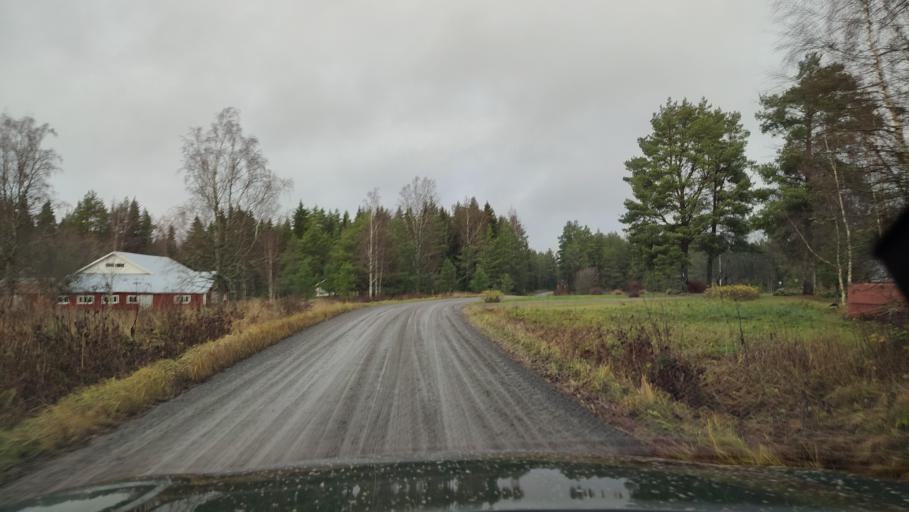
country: FI
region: Ostrobothnia
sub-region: Sydosterbotten
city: Naerpes
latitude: 62.4628
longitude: 21.4895
